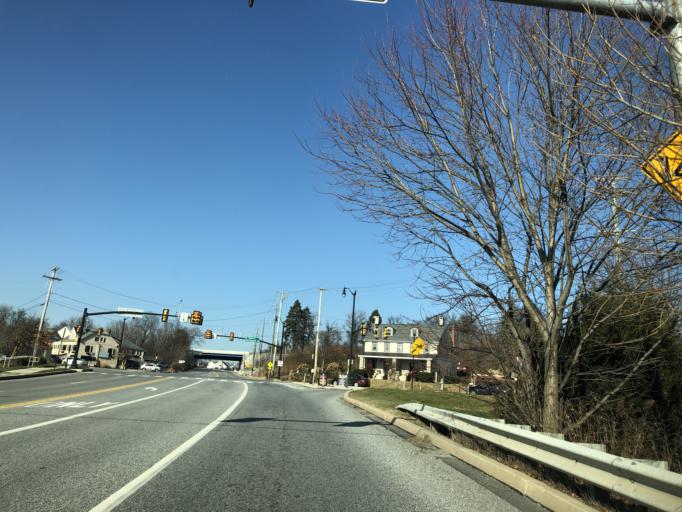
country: US
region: Pennsylvania
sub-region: Chester County
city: Malvern
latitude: 40.0742
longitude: -75.5357
